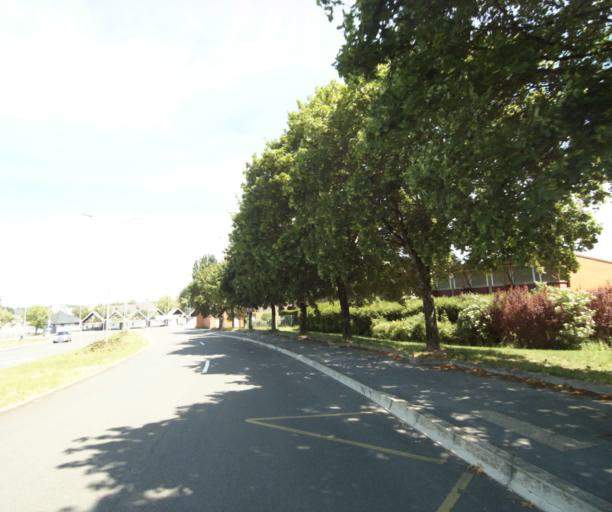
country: FR
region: Champagne-Ardenne
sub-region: Departement des Ardennes
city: Charleville-Mezieres
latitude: 49.7557
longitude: 4.7085
